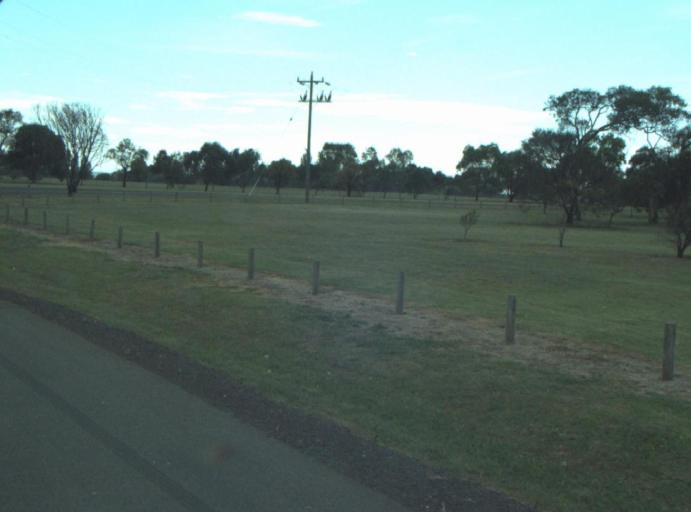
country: AU
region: Victoria
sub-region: Greater Geelong
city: Leopold
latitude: -38.1565
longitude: 144.4430
